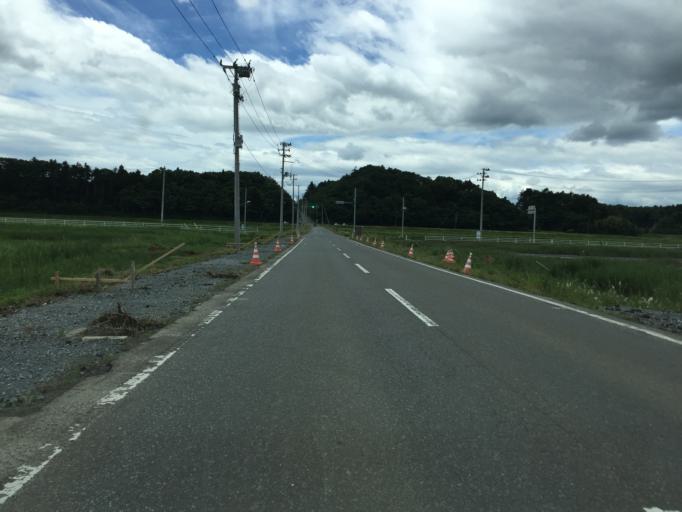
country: JP
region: Fukushima
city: Namie
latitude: 37.6804
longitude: 141.0040
